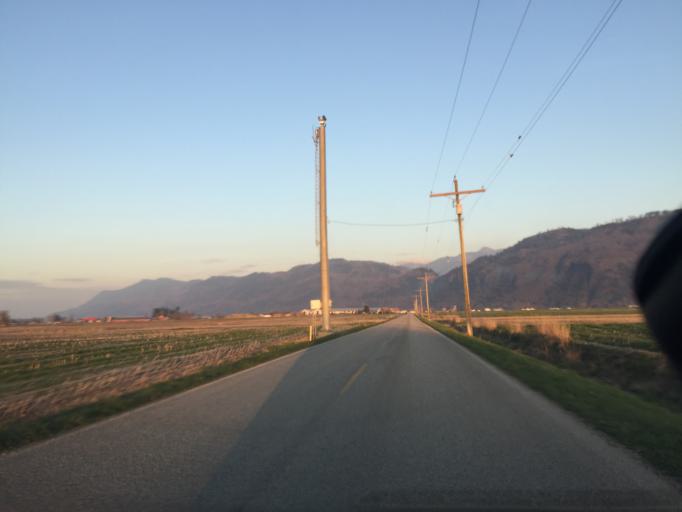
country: US
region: Washington
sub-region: Whatcom County
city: Sumas
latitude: 48.9999
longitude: -122.2108
